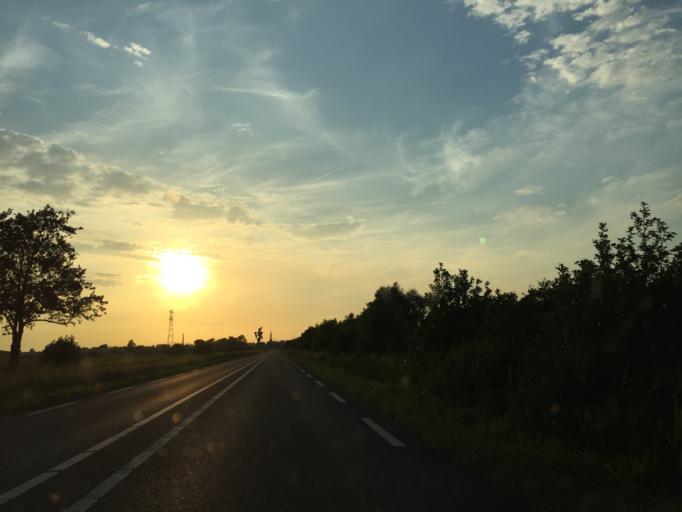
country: NL
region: South Holland
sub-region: Gemeente Gouda
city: Gouda
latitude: 51.9984
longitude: 4.7342
